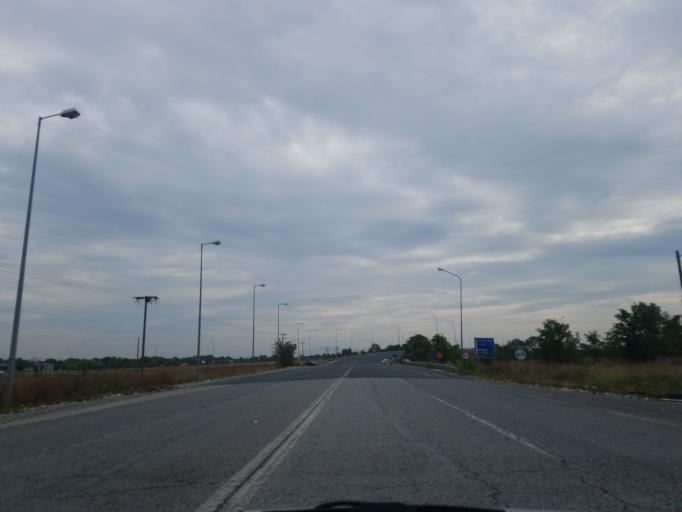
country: GR
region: Thessaly
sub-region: Nomos Kardhitsas
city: Sofades
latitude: 39.3446
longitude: 22.0781
